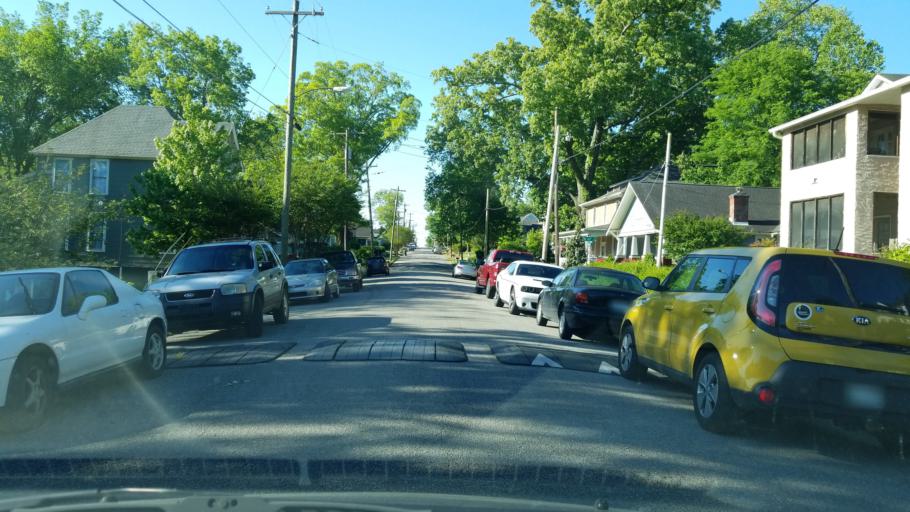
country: US
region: Tennessee
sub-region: Hamilton County
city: Lookout Mountain
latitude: 35.0027
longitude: -85.3301
